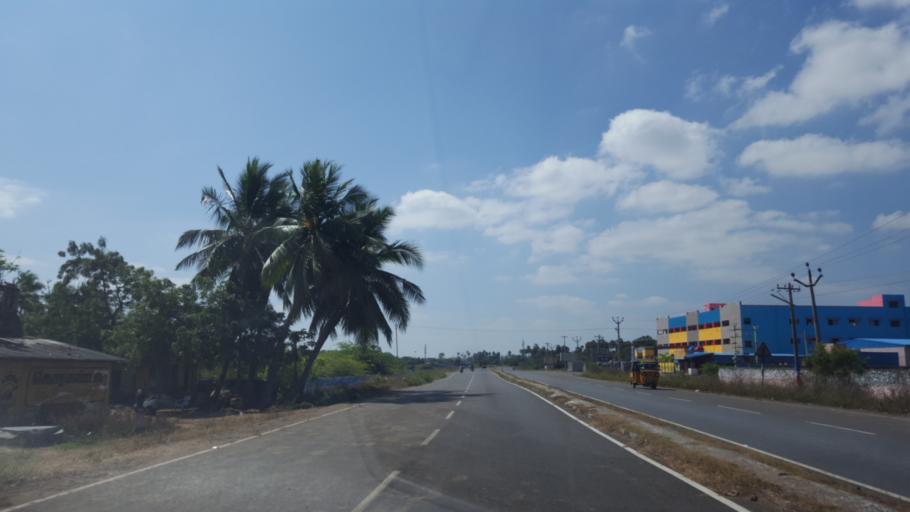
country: IN
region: Tamil Nadu
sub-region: Kancheepuram
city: Mamallapuram
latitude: 12.6249
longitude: 80.1709
